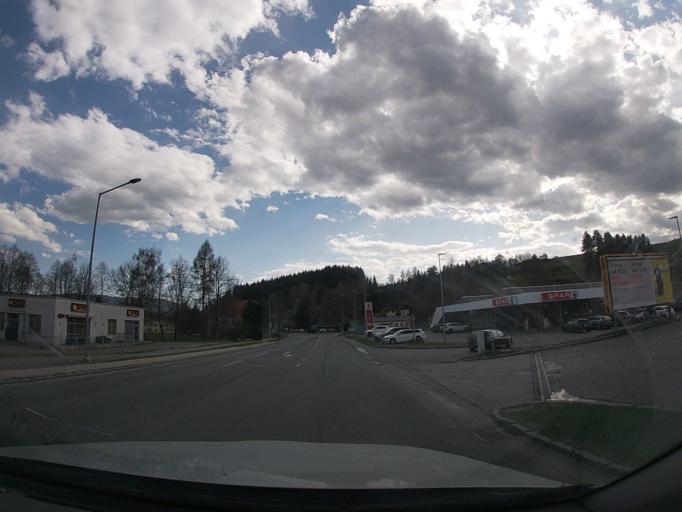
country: AT
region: Styria
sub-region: Politischer Bezirk Murau
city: Neumarkt in Steiermark
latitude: 47.0791
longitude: 14.4248
